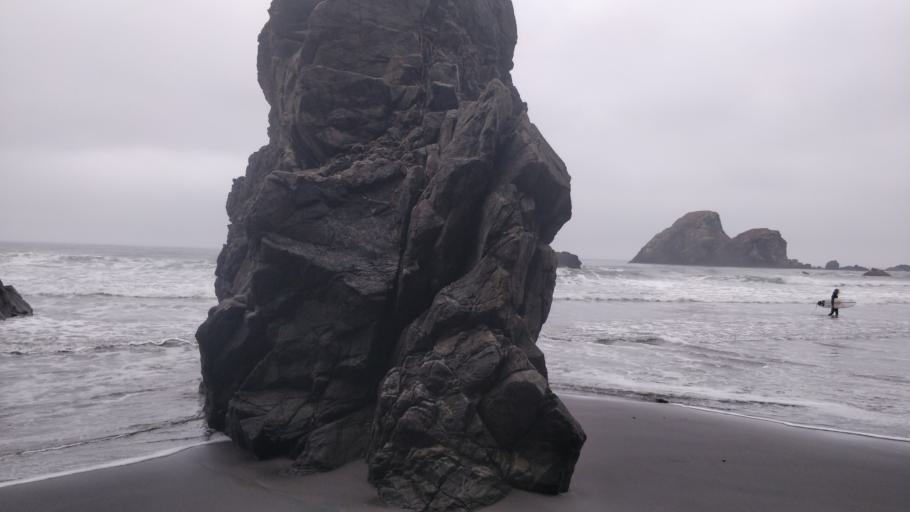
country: US
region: California
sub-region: Humboldt County
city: Westhaven-Moonstone
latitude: 41.0350
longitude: -124.1174
